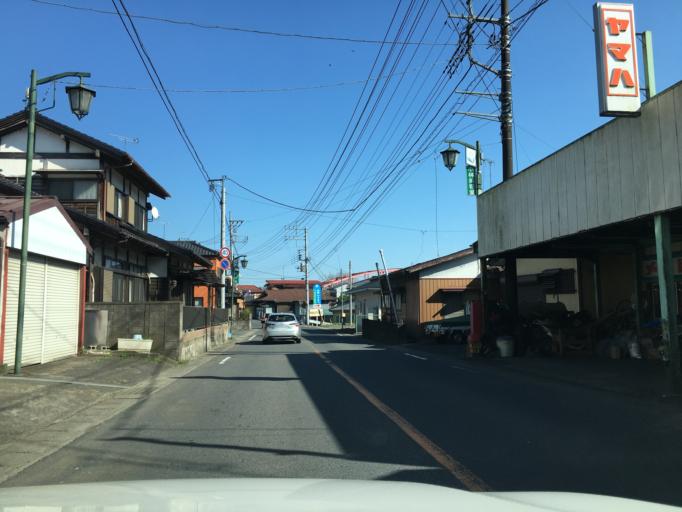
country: JP
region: Ibaraki
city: Omiya
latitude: 36.5489
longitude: 140.3299
